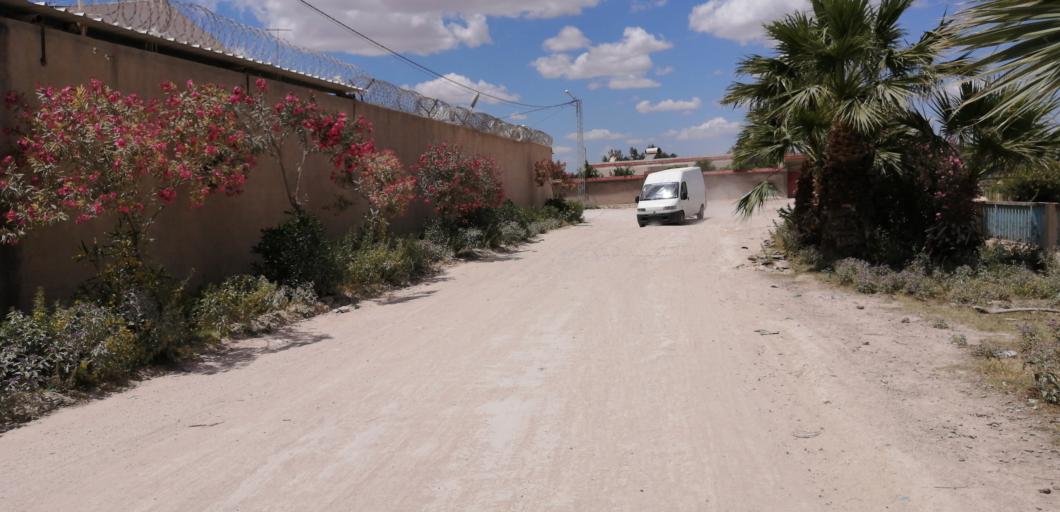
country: TN
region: Al Qayrawan
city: Kairouan
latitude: 35.6228
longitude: 9.9228
